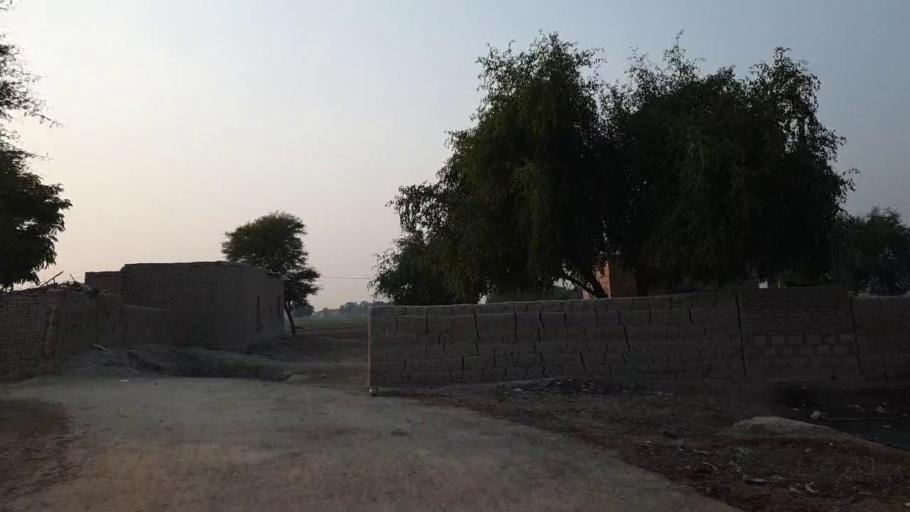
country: PK
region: Sindh
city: Bhan
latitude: 26.4938
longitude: 67.7373
